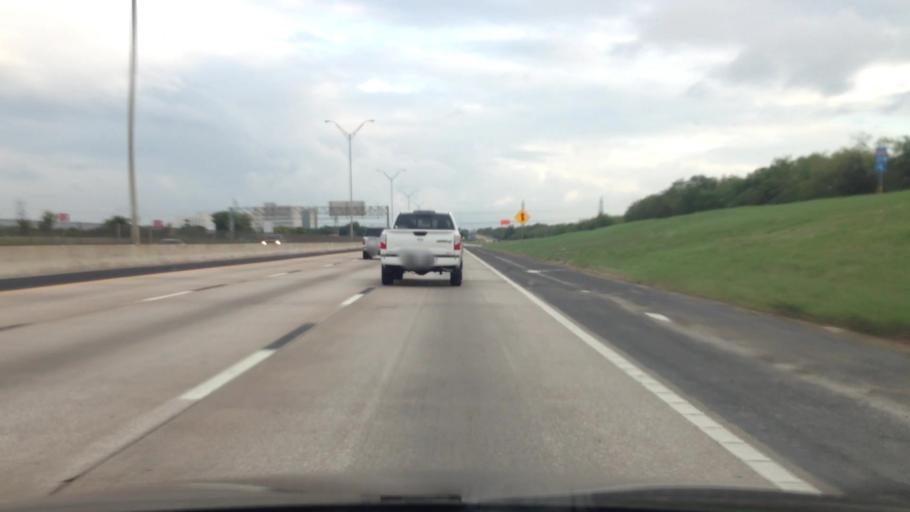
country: US
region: Texas
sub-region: Tarrant County
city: Everman
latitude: 32.5962
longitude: -97.3196
